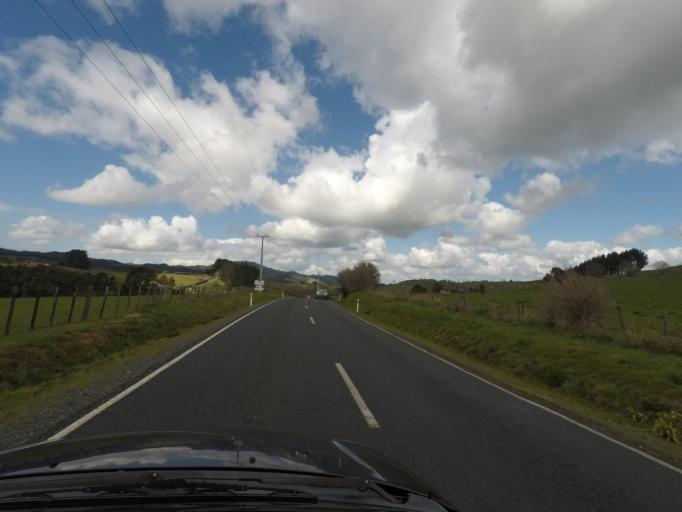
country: NZ
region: Auckland
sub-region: Auckland
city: Red Hill
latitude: -37.1162
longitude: 175.1090
